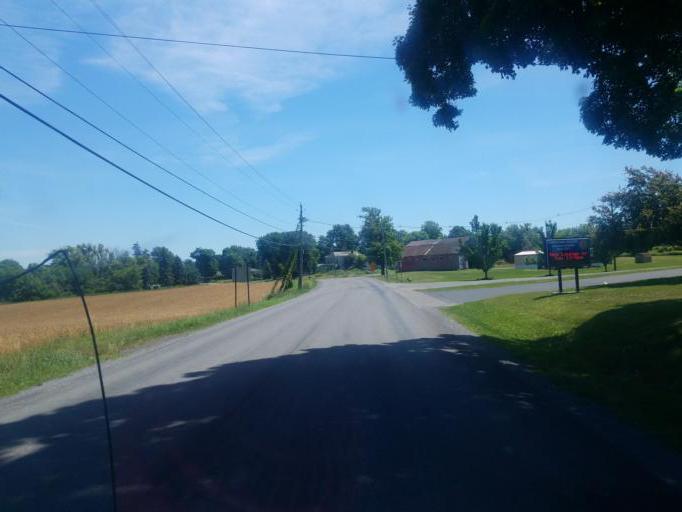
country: US
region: New York
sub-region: Yates County
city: Penn Yan
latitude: 42.6525
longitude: -77.0400
